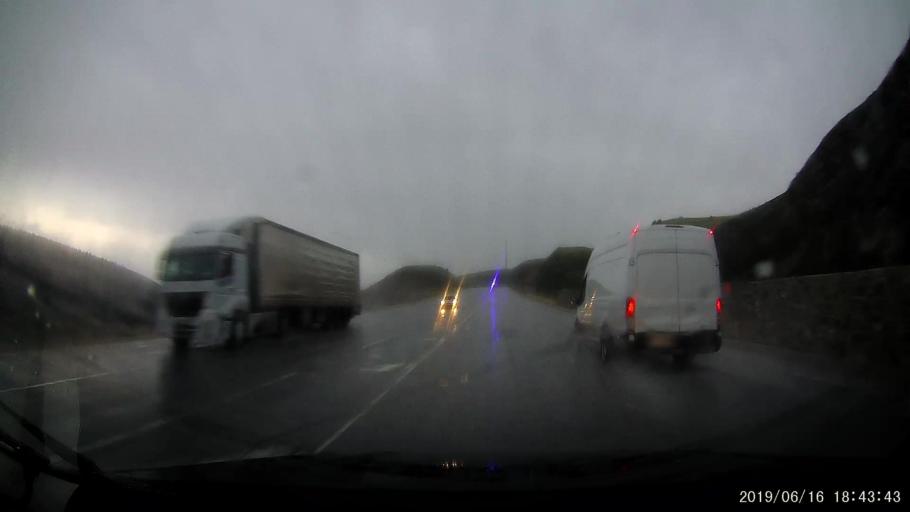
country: TR
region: Erzincan
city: Doganbeyli
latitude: 39.8717
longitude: 39.0877
